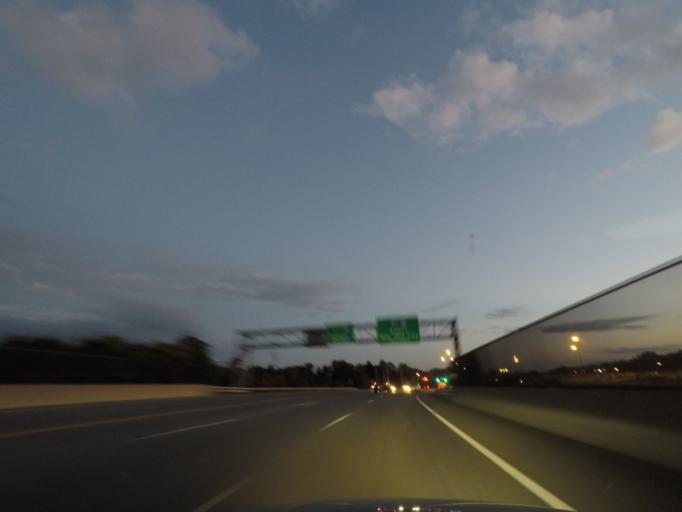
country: US
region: New York
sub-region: Orange County
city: Gardnertown
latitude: 41.5144
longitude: -74.0669
